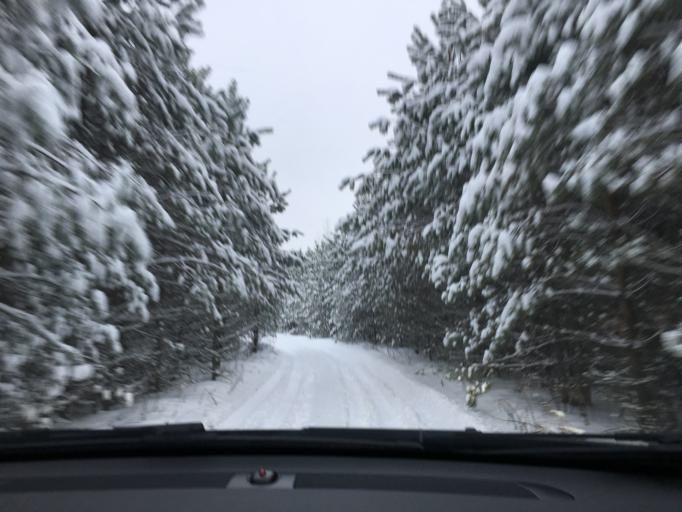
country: LT
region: Alytaus apskritis
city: Druskininkai
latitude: 53.9199
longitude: 24.1946
